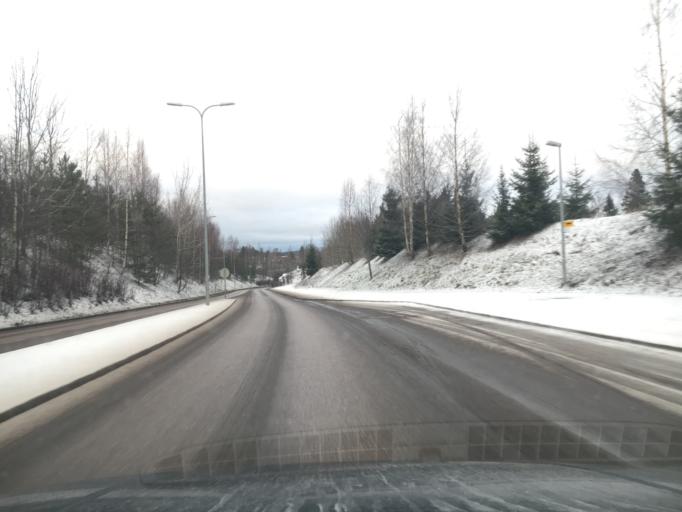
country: FI
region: Uusimaa
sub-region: Helsinki
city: Espoo
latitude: 60.1631
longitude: 24.6602
